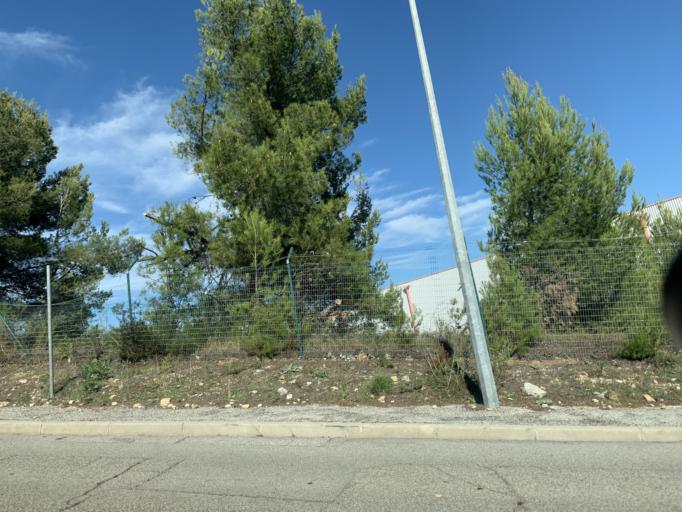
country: FR
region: Provence-Alpes-Cote d'Azur
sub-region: Departement des Bouches-du-Rhone
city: La Ciotat
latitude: 43.2042
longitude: 5.5979
